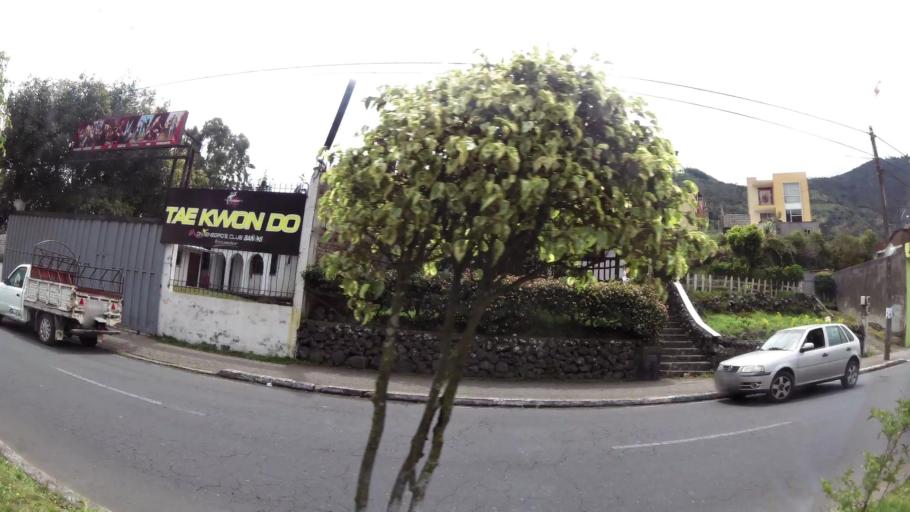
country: EC
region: Tungurahua
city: Banos
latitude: -1.3919
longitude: -78.4168
